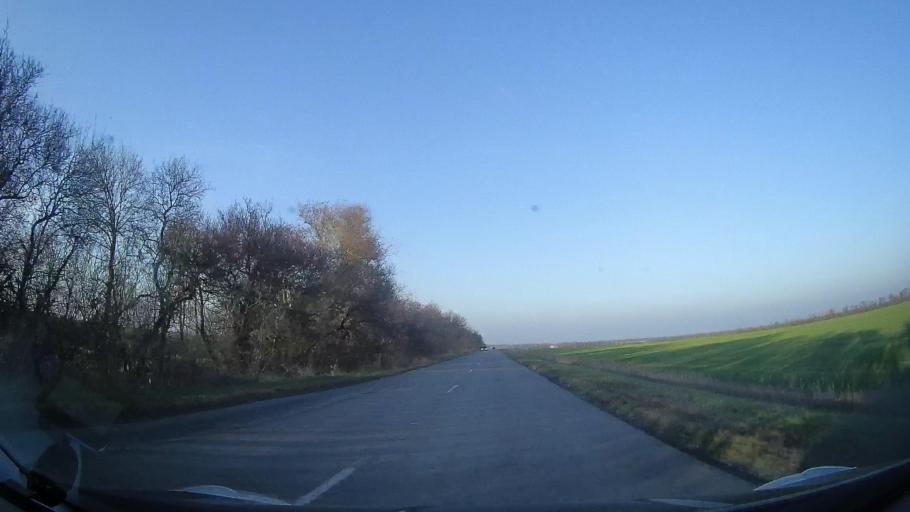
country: RU
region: Rostov
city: Kirovskaya
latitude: 47.0160
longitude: 39.9789
